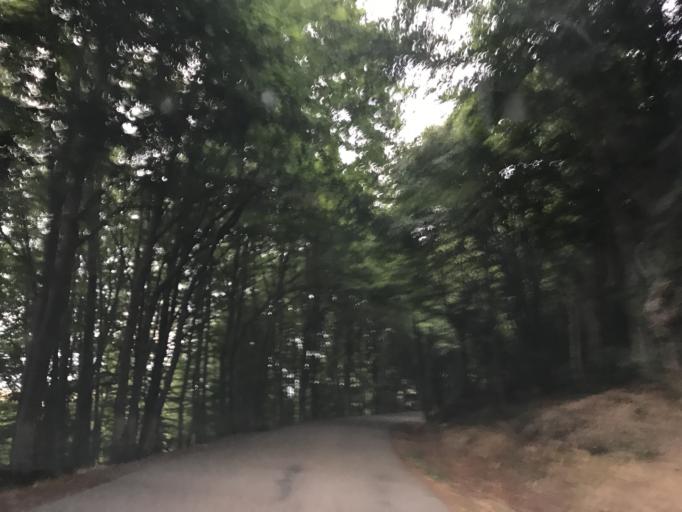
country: FR
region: Auvergne
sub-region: Departement du Puy-de-Dome
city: Thiers
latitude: 45.8423
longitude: 3.5725
